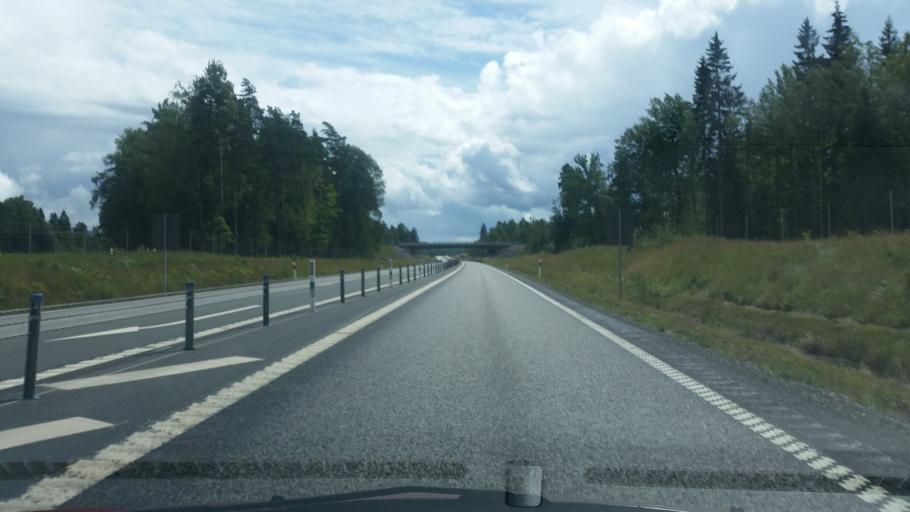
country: SE
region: Joenkoeping
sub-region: Gislaveds Kommun
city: Gislaved
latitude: 57.2918
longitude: 13.5938
